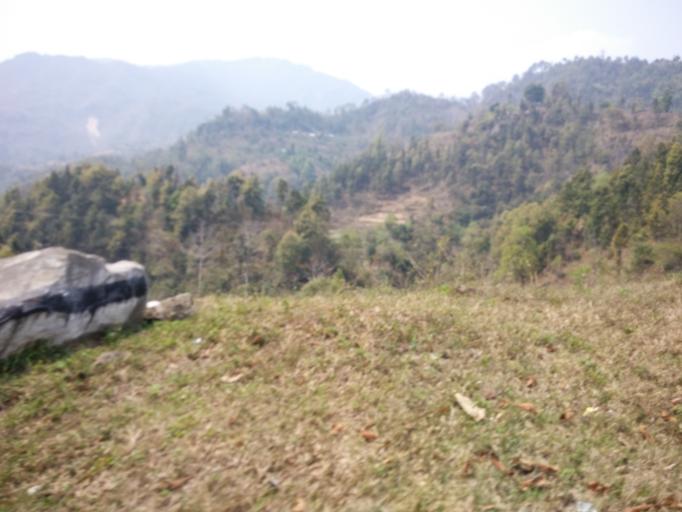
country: NP
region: Central Region
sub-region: Narayani Zone
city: Hitura
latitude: 27.5270
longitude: 85.0462
